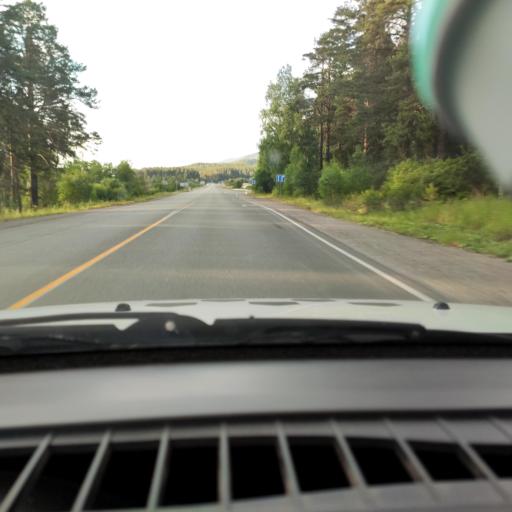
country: RU
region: Chelyabinsk
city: Turgoyak
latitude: 55.2234
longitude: 60.1865
